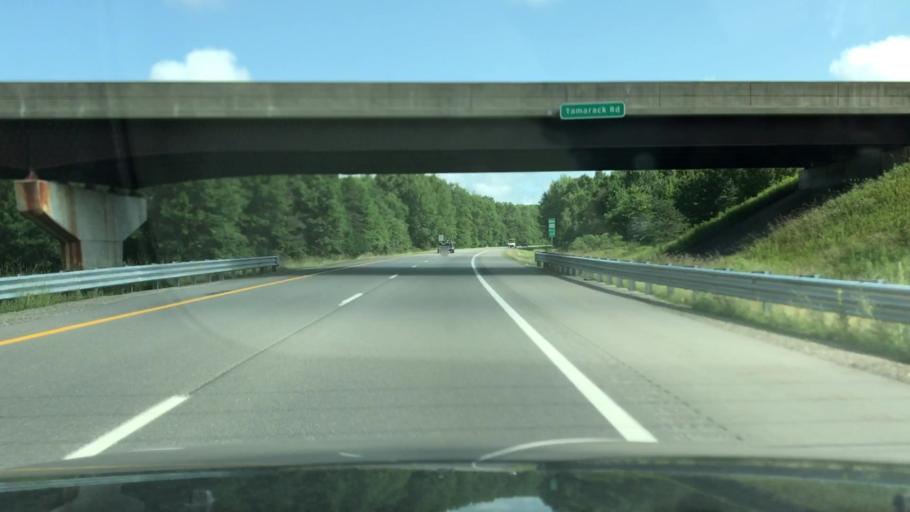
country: US
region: Michigan
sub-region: Montcalm County
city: Howard City
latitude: 43.4390
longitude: -85.4923
